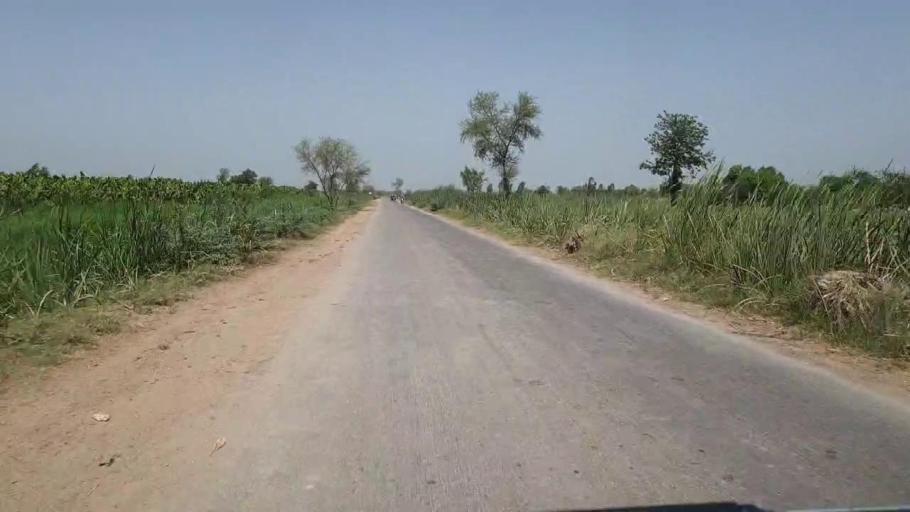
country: PK
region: Sindh
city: Nawabshah
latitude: 26.3424
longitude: 68.3772
